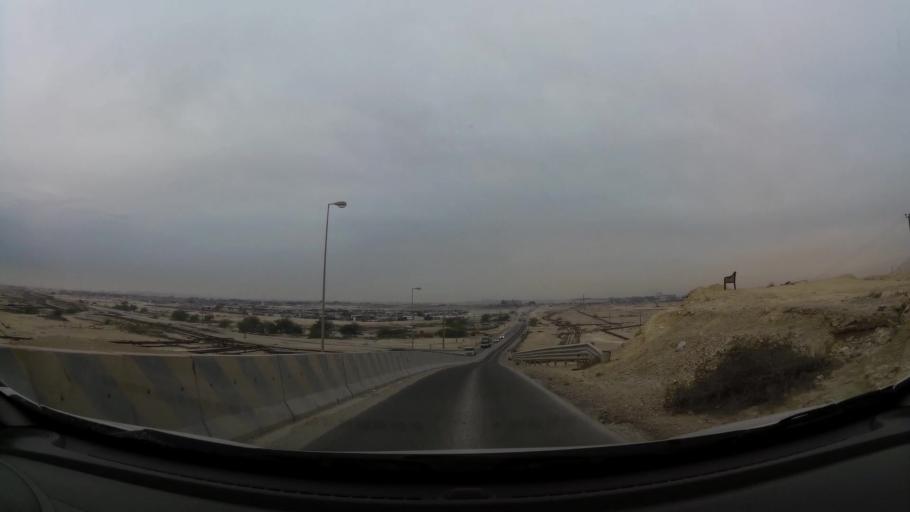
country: BH
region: Northern
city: Ar Rifa'
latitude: 26.0908
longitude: 50.5837
